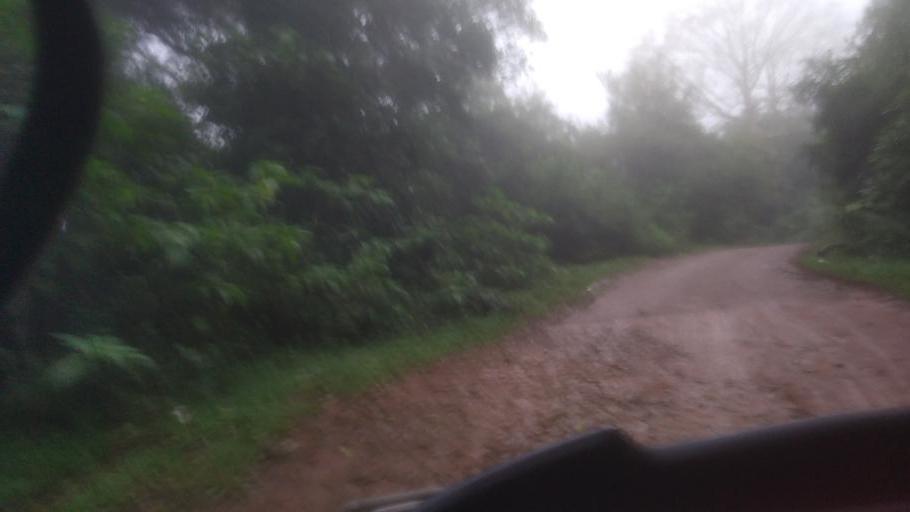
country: IN
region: Tamil Nadu
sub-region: Theni
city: Kombai
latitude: 9.8909
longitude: 77.2192
